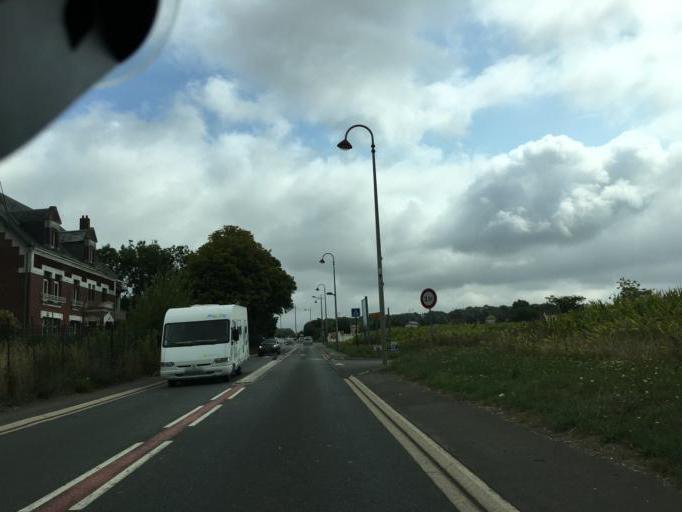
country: FR
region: Nord-Pas-de-Calais
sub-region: Departement du Pas-de-Calais
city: Rang-du-Fliers
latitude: 50.4182
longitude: 1.6518
